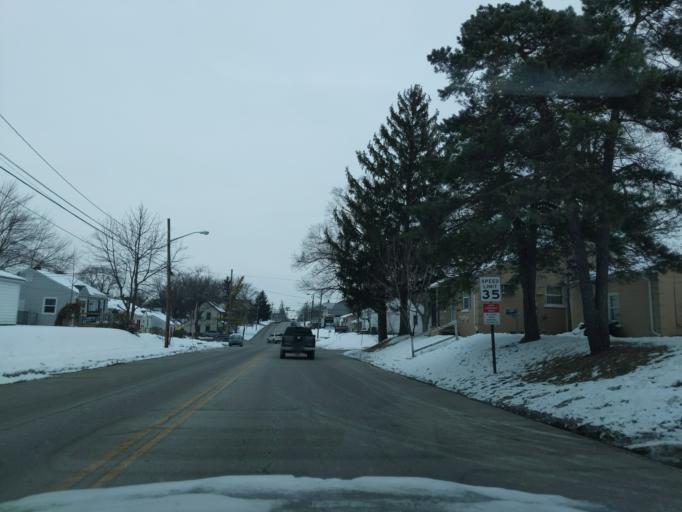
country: US
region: Indiana
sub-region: Tippecanoe County
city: Lafayette
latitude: 40.4137
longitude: -86.8772
